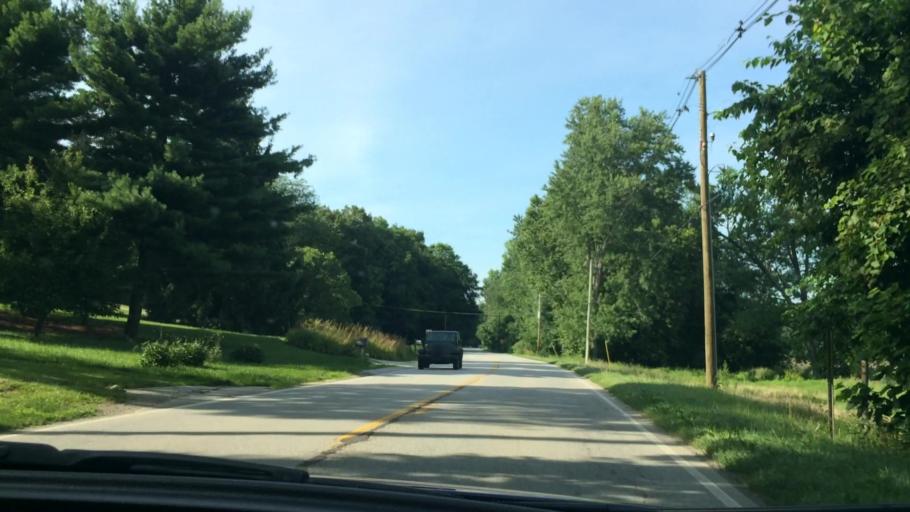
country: US
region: Indiana
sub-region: Tippecanoe County
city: West Lafayette
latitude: 40.4444
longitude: -86.8966
